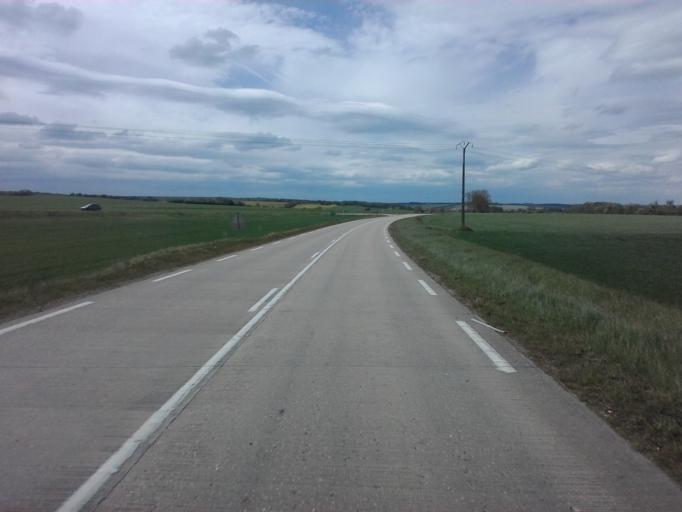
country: FR
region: Bourgogne
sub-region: Departement de l'Yonne
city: Saint-Bris-le-Vineux
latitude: 47.6896
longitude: 3.6516
